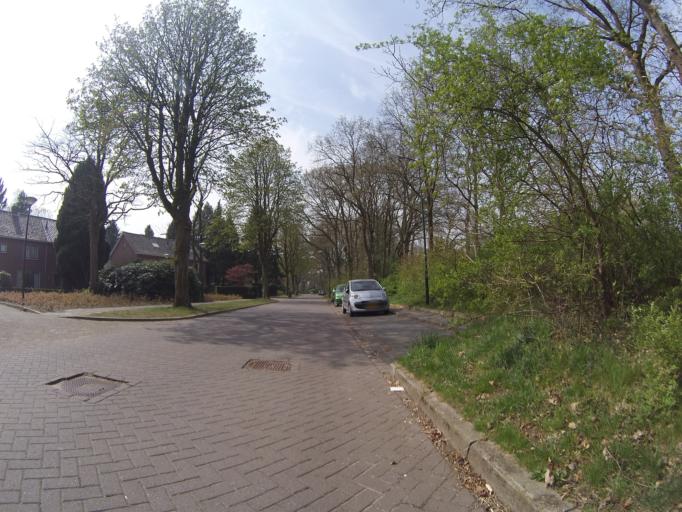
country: NL
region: Utrecht
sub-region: Gemeente Soest
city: Soest
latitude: 52.1624
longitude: 5.2988
